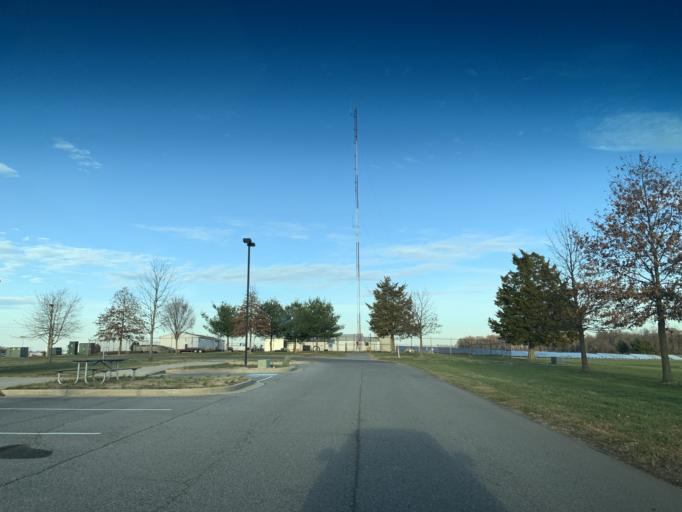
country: US
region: Maryland
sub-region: Kent County
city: Chestertown
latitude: 39.2813
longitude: -76.0917
